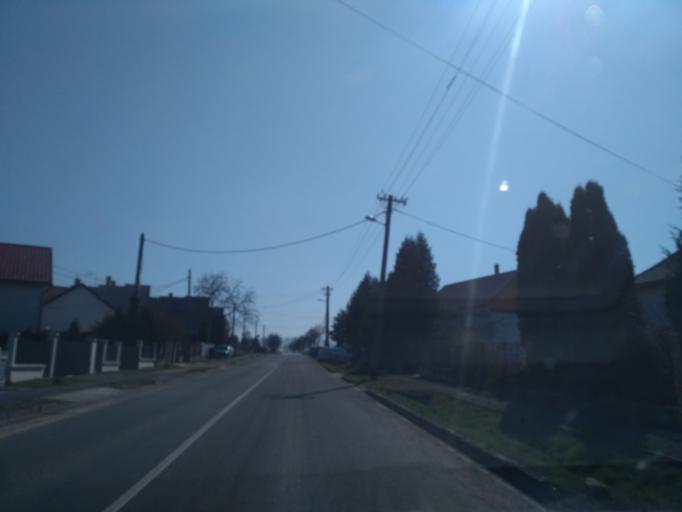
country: SK
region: Kosicky
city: Secovce
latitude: 48.6977
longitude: 21.6389
